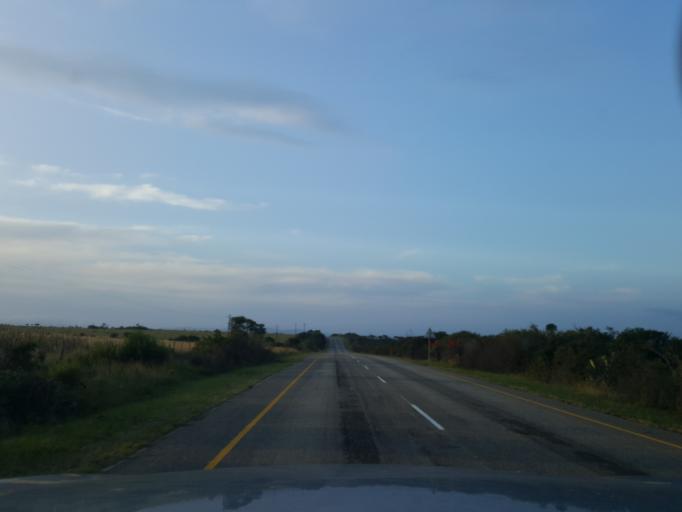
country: ZA
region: Eastern Cape
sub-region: Cacadu District Municipality
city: Grahamstown
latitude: -33.4906
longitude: 26.4869
